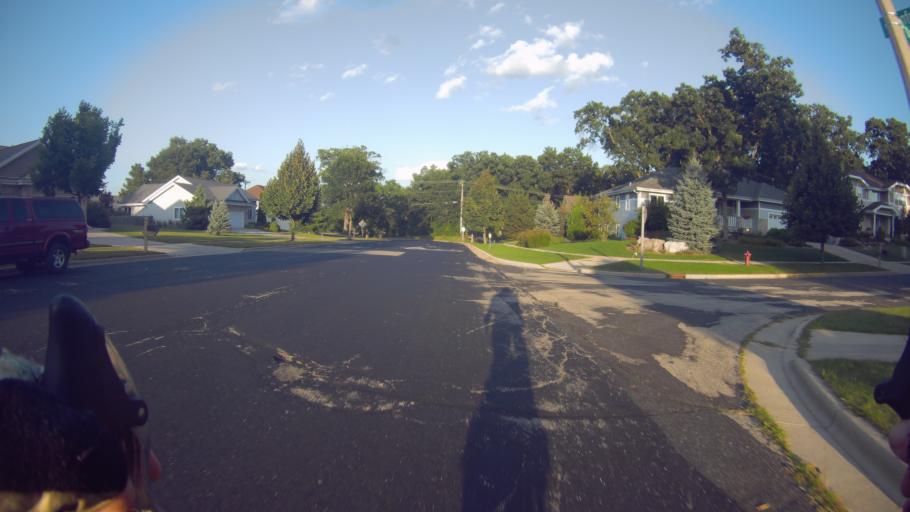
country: US
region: Wisconsin
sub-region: Dane County
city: Madison
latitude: 43.0223
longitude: -89.4267
